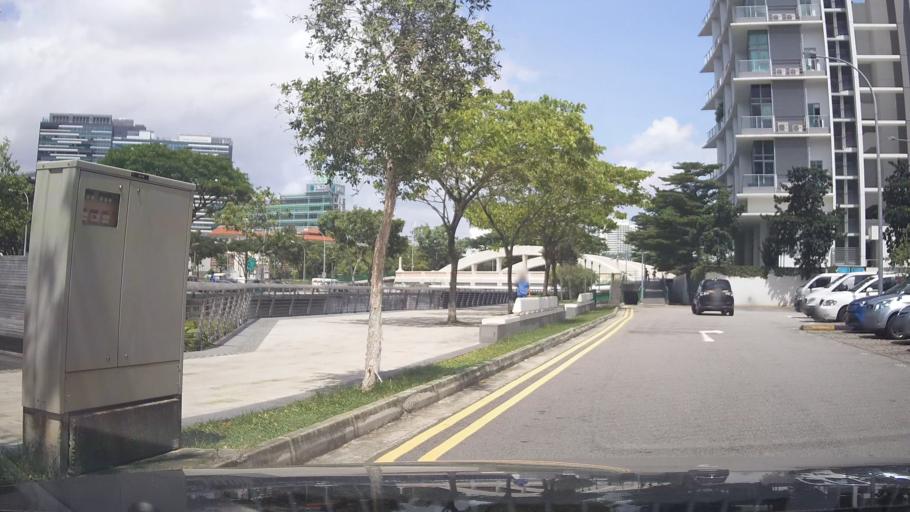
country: SG
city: Singapore
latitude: 1.3060
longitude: 103.8635
